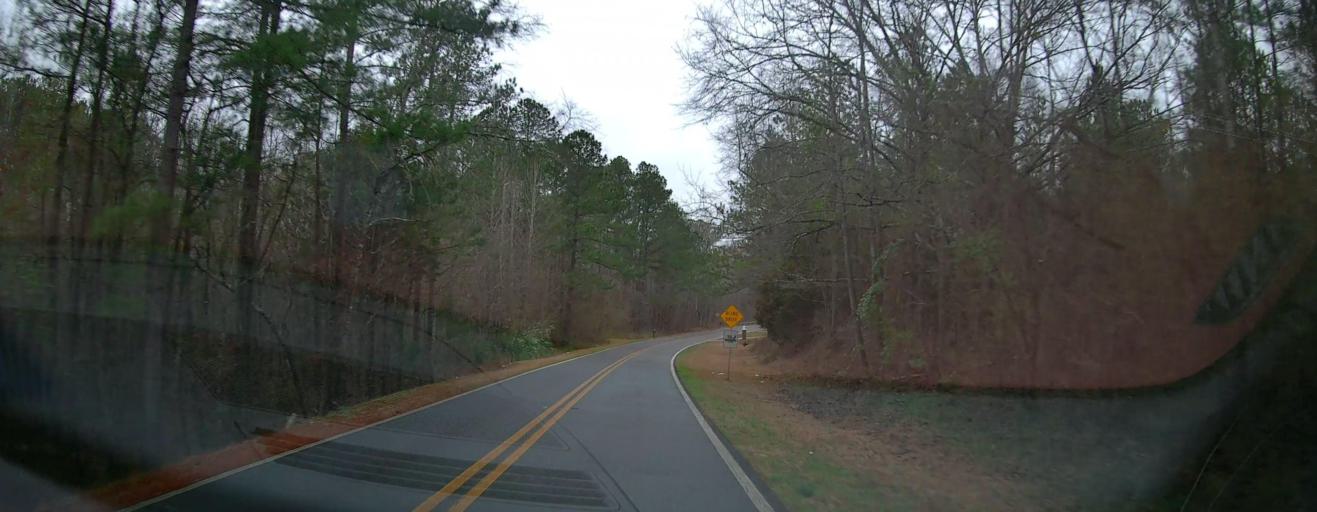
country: US
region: Georgia
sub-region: Monroe County
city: Forsyth
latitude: 33.1120
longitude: -83.9458
